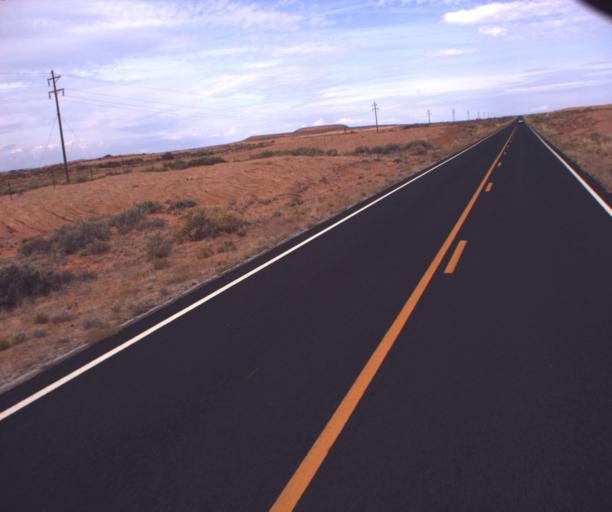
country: US
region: Arizona
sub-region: Apache County
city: Many Farms
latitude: 36.8138
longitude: -109.6465
